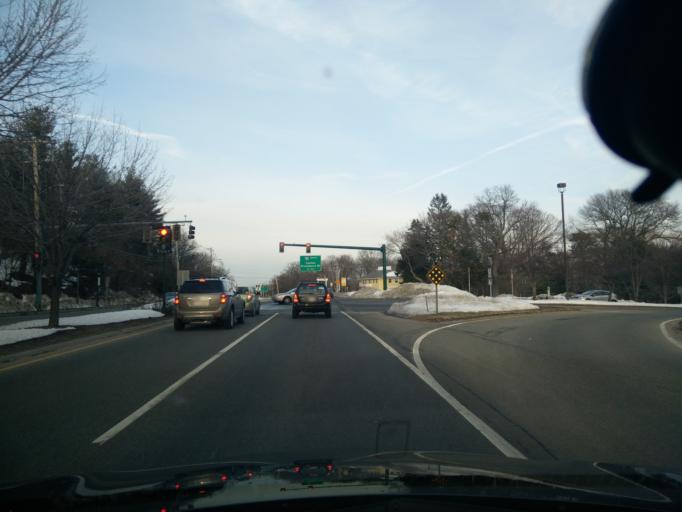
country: US
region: Massachusetts
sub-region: Norfolk County
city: Westwood
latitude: 42.2409
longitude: -71.2117
